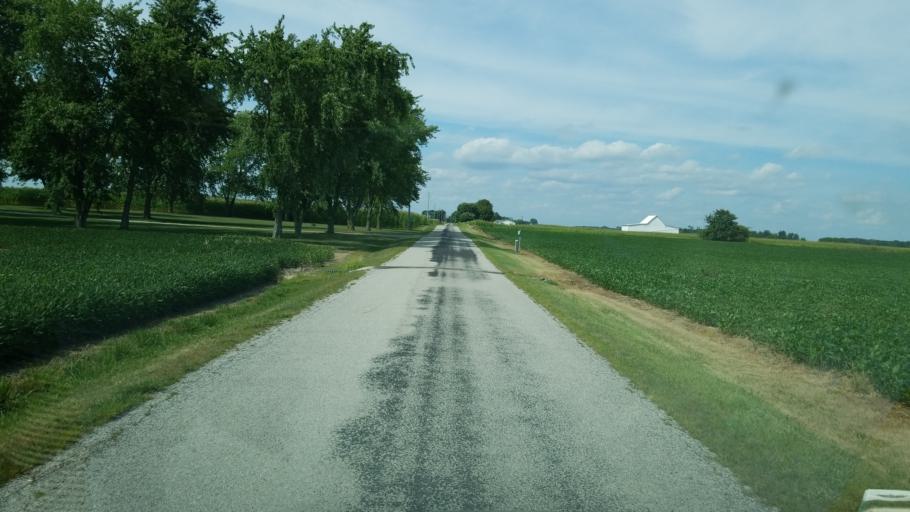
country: US
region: Ohio
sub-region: Marion County
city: Prospect
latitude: 40.4563
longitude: -83.1254
